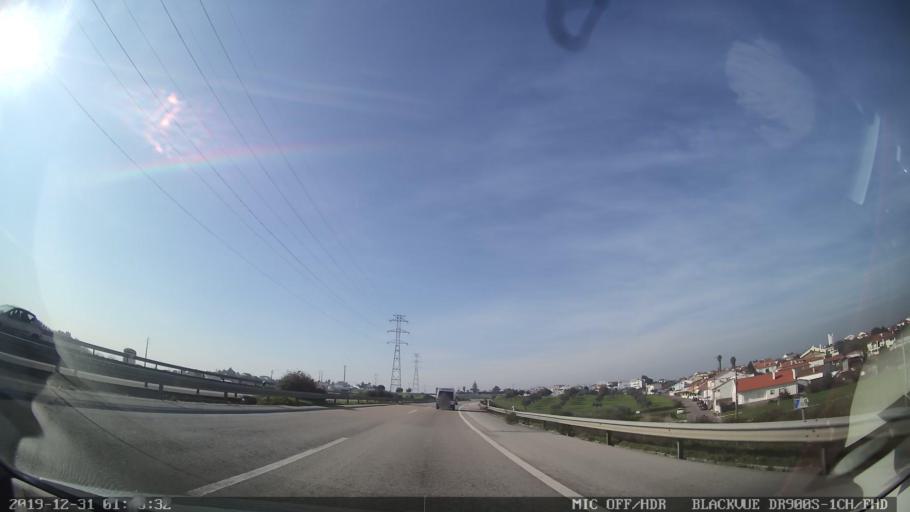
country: PT
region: Santarem
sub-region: Entroncamento
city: Entroncamento
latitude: 39.4707
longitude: -8.4951
